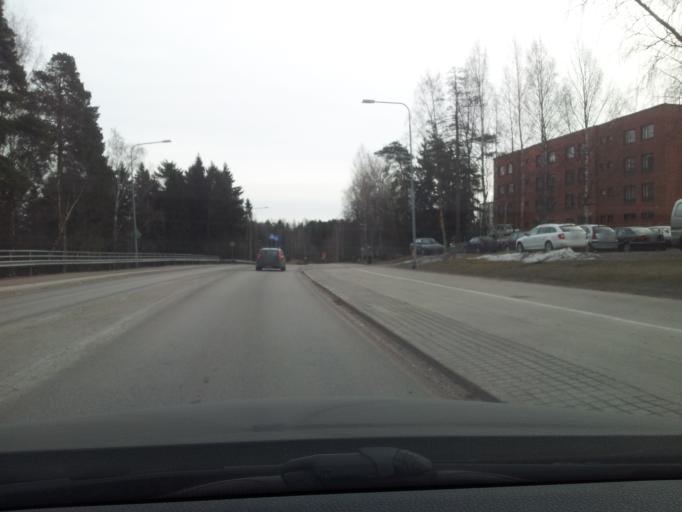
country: FI
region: Uusimaa
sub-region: Helsinki
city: Kauniainen
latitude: 60.1777
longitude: 24.7364
